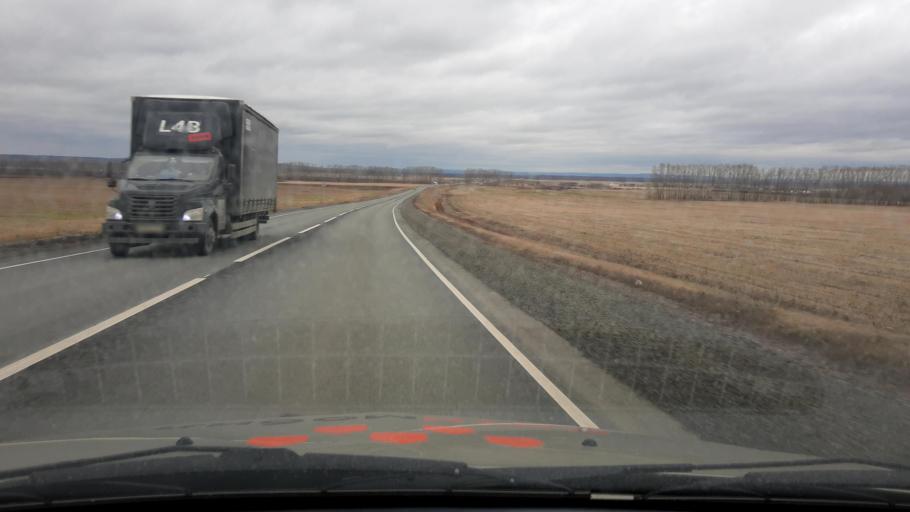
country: RU
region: Bashkortostan
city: Avdon
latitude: 54.8598
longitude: 55.7038
